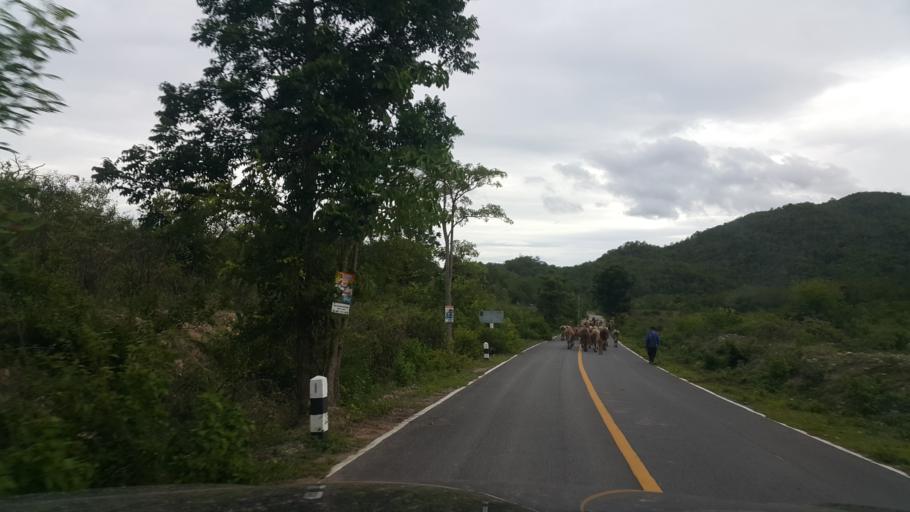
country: TH
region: Sukhothai
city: Thung Saliam
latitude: 17.1788
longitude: 99.4831
